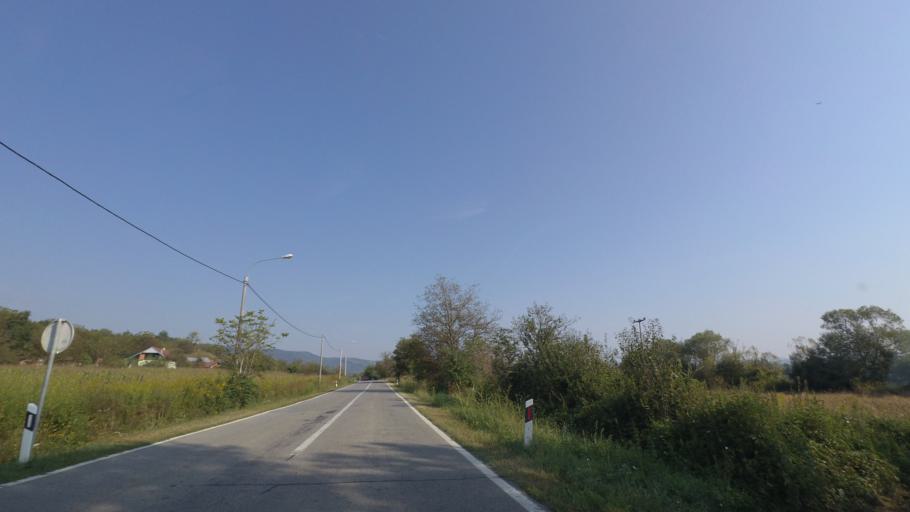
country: HR
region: Brodsko-Posavska
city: Resetari
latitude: 45.3860
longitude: 17.5100
